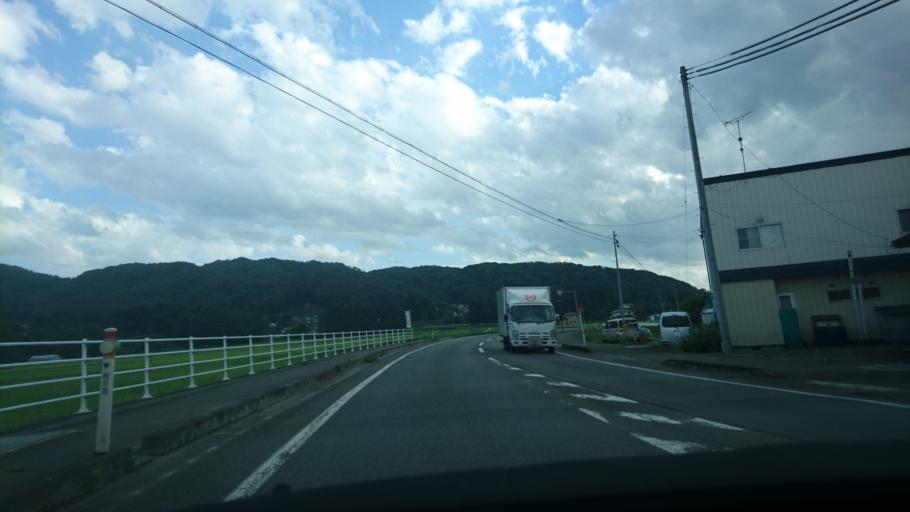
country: JP
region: Iwate
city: Kitakami
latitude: 39.2831
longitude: 141.1371
